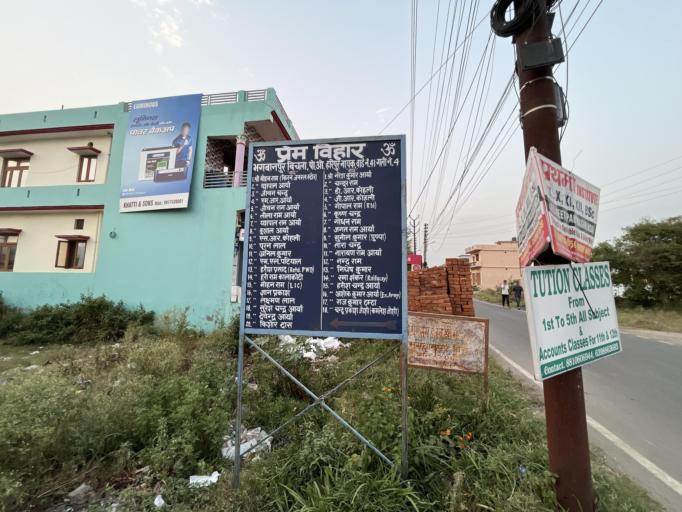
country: IN
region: Uttarakhand
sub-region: Naini Tal
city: Haldwani
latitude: 29.2210
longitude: 79.4769
